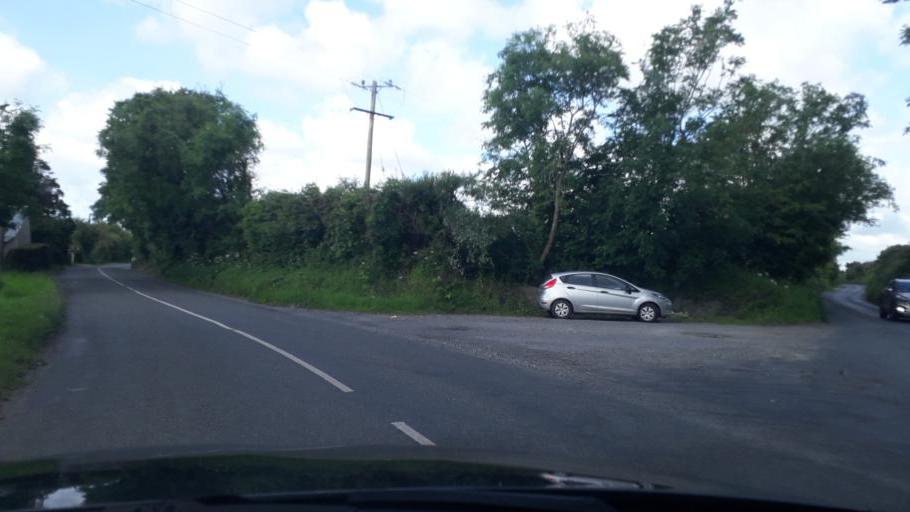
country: IE
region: Leinster
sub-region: Loch Garman
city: Loch Garman
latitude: 52.2829
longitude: -6.5381
